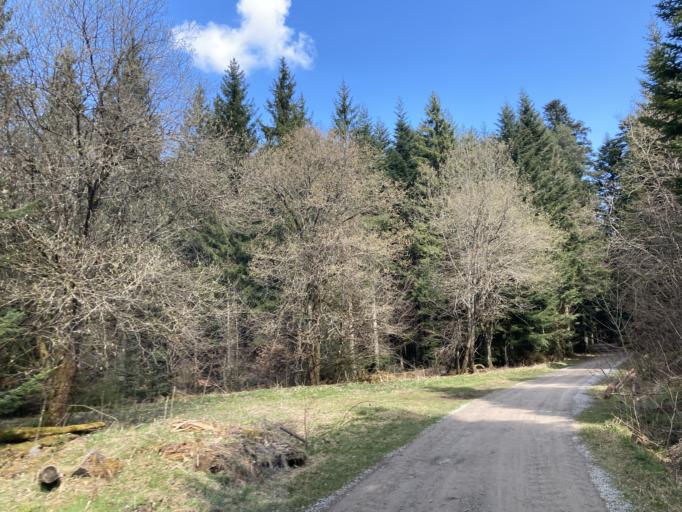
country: DE
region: Baden-Wuerttemberg
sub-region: Karlsruhe Region
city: Schomberg
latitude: 48.7871
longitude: 8.6279
